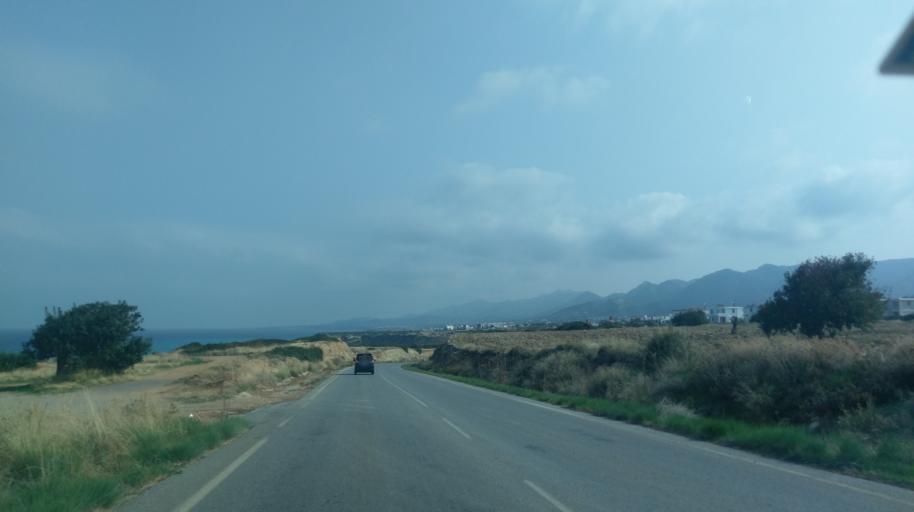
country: CY
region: Ammochostos
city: Lefkonoiko
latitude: 35.3539
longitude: 33.6111
